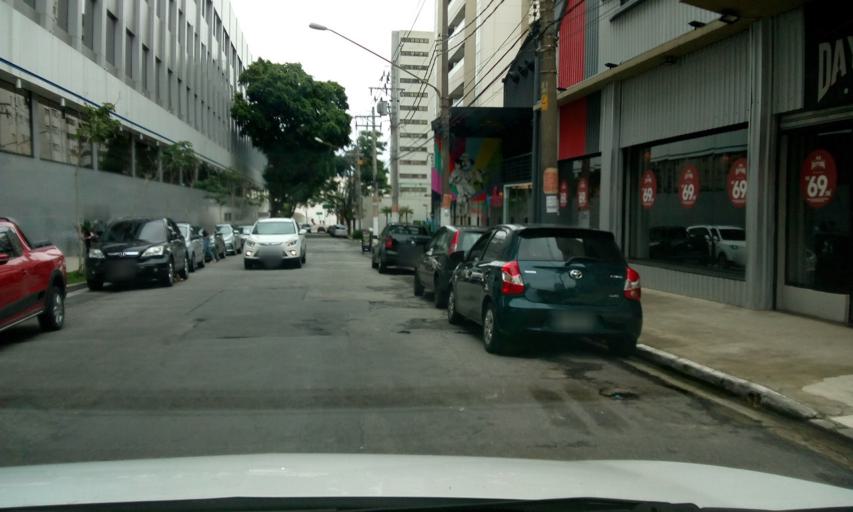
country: BR
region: Sao Paulo
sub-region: Sao Paulo
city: Sao Paulo
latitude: -23.5286
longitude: -46.6644
